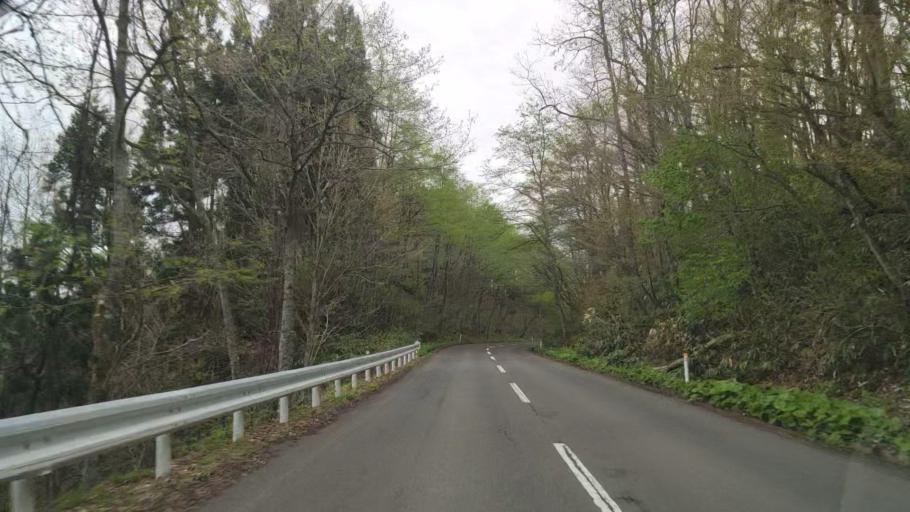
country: JP
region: Akita
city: Hanawa
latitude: 40.3789
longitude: 140.7913
